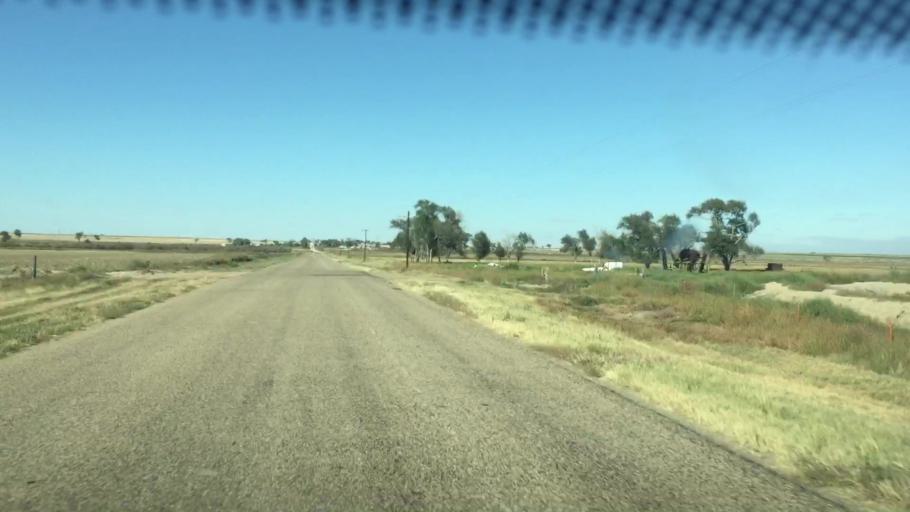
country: US
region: Colorado
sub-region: Prowers County
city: Lamar
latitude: 38.1065
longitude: -102.5214
